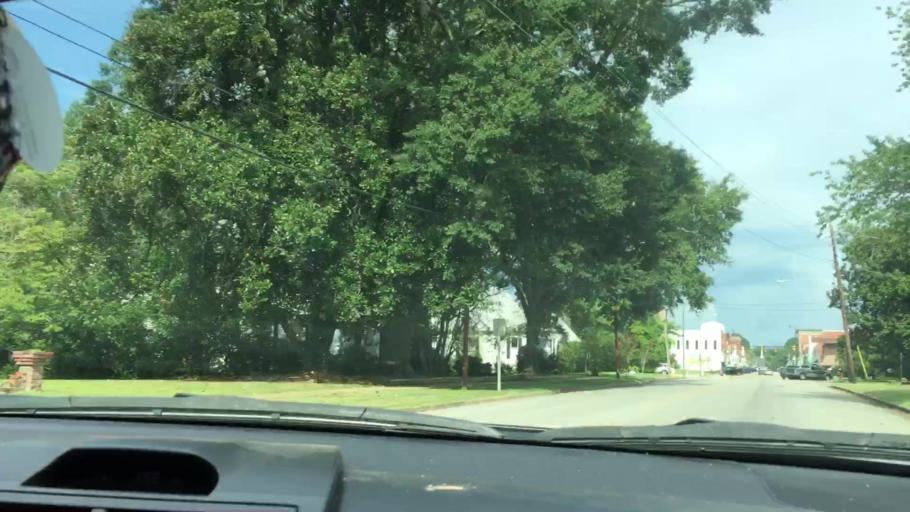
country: US
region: Alabama
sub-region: Hale County
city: Greensboro
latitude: 32.7041
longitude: -87.5982
